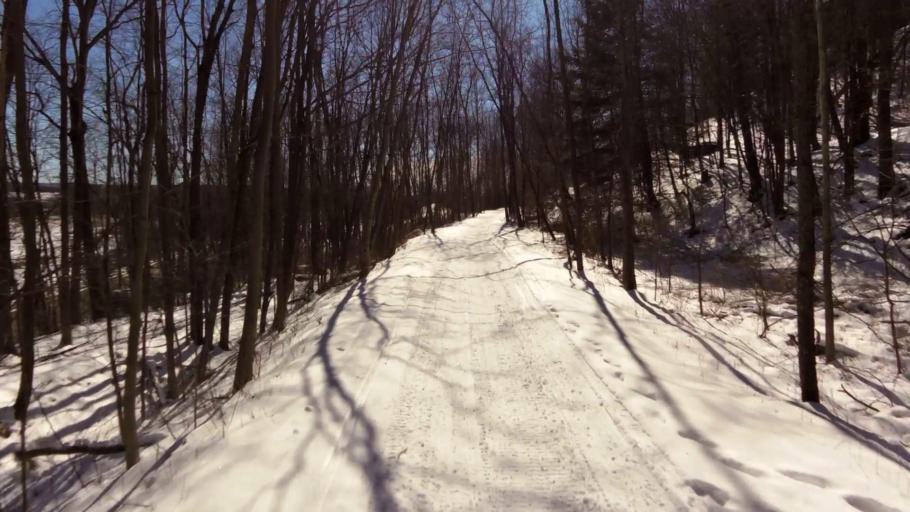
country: US
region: New York
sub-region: Allegany County
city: Houghton
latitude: 42.3551
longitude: -78.1267
